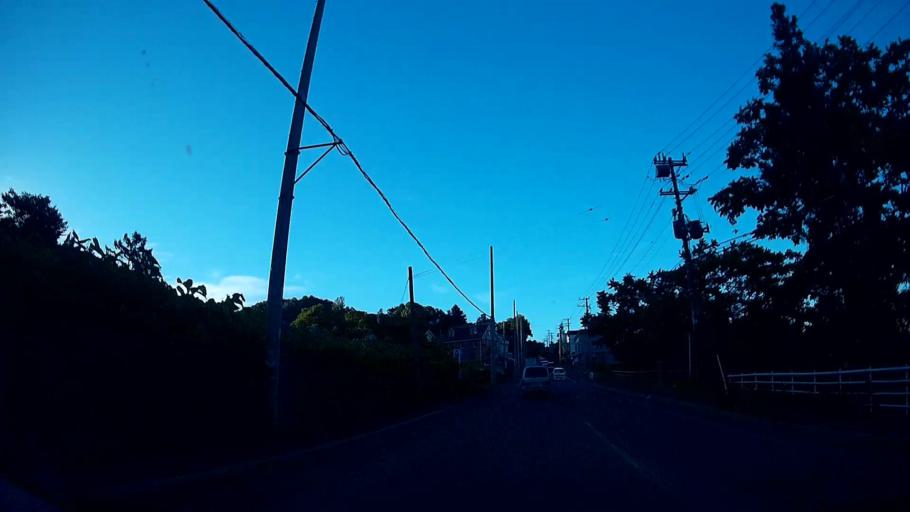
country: JP
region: Hokkaido
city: Otaru
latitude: 43.1703
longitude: 140.9904
